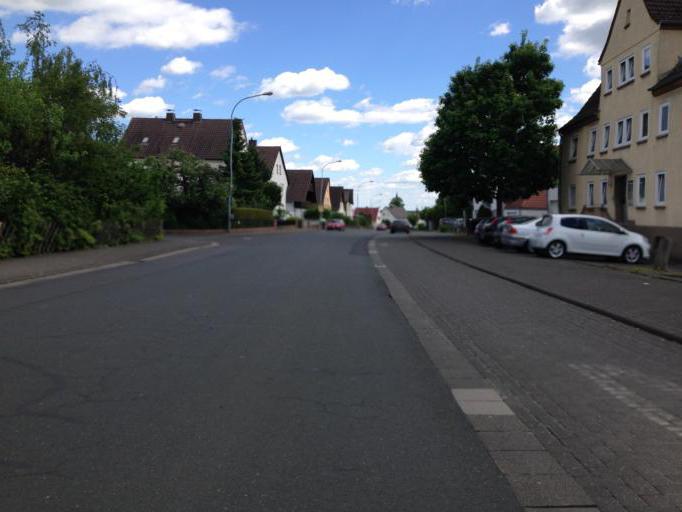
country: DE
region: Hesse
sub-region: Regierungsbezirk Giessen
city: Heuchelheim
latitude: 50.5856
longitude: 8.6224
